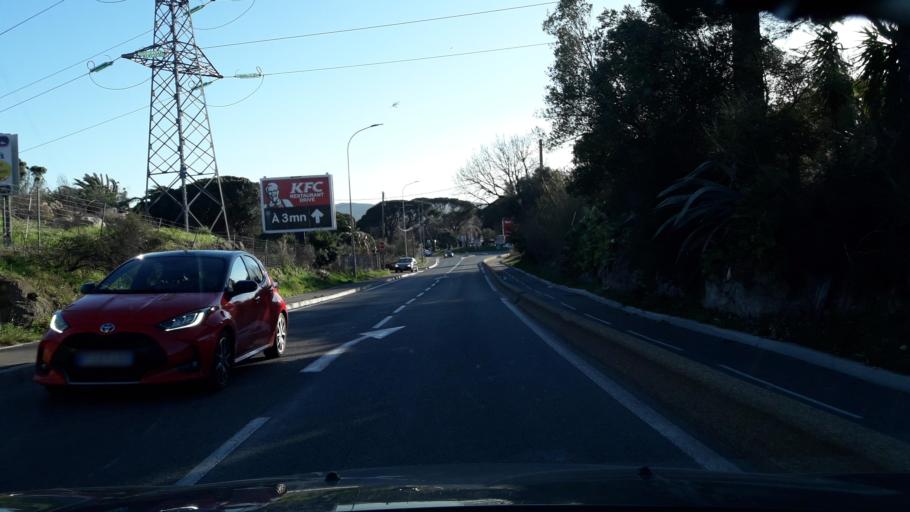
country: FR
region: Provence-Alpes-Cote d'Azur
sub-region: Departement du Var
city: Frejus
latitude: 43.4453
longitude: 6.7264
